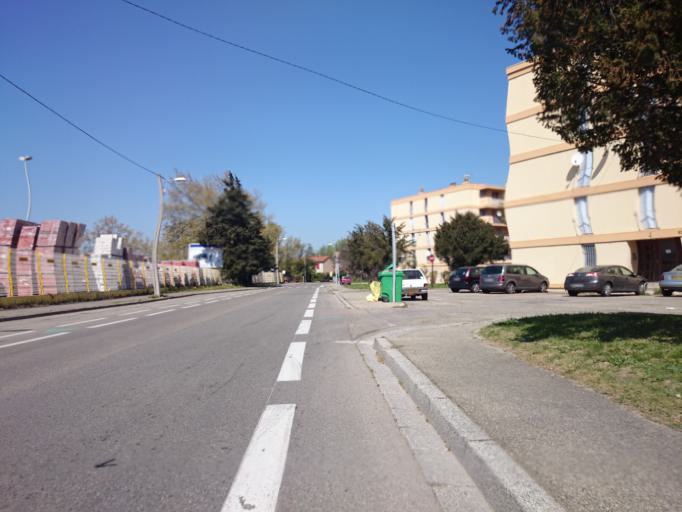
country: FR
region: Provence-Alpes-Cote d'Azur
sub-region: Departement du Vaucluse
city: Avignon
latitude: 43.9313
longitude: 4.7967
